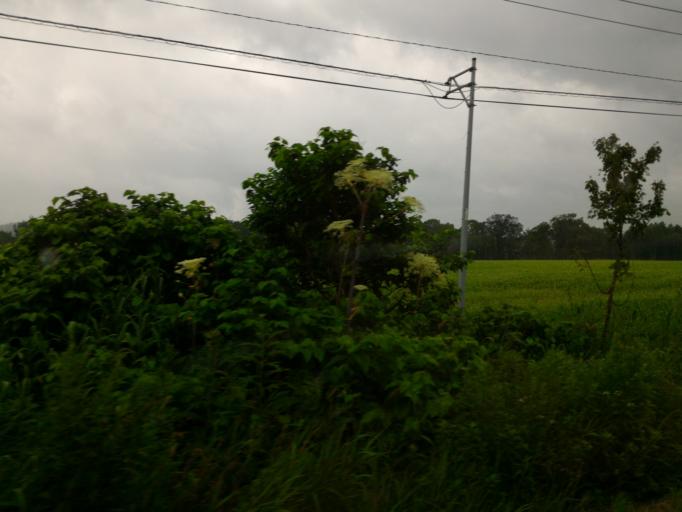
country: JP
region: Hokkaido
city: Nayoro
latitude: 44.6533
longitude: 142.2678
